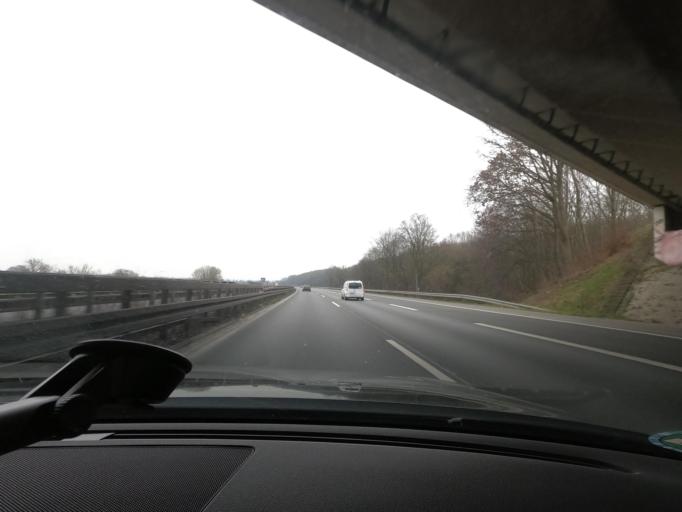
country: DE
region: North Rhine-Westphalia
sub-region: Regierungsbezirk Dusseldorf
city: Viersen
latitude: 51.2732
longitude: 6.3493
